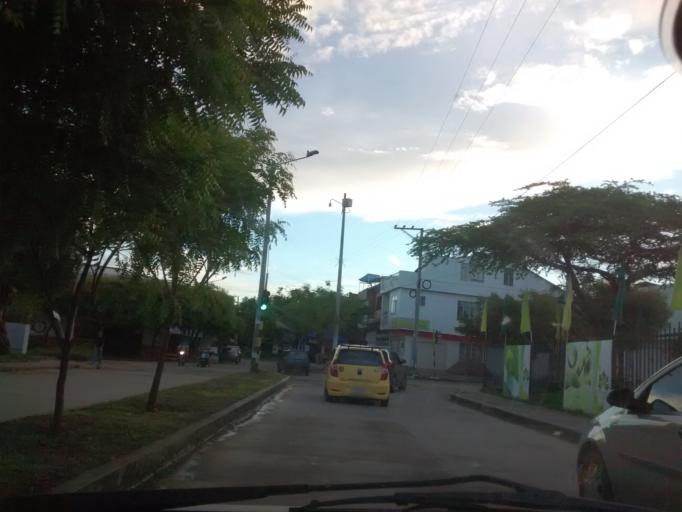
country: CO
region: Cundinamarca
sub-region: Girardot
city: Girardot City
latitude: 4.3153
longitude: -74.7930
